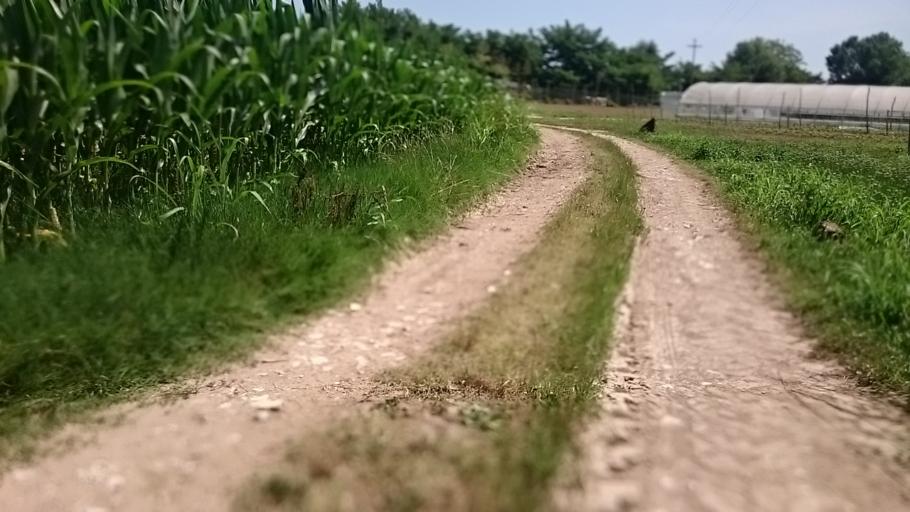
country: IT
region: Veneto
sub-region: Provincia di Vicenza
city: Vicenza
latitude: 45.5314
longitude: 11.5675
